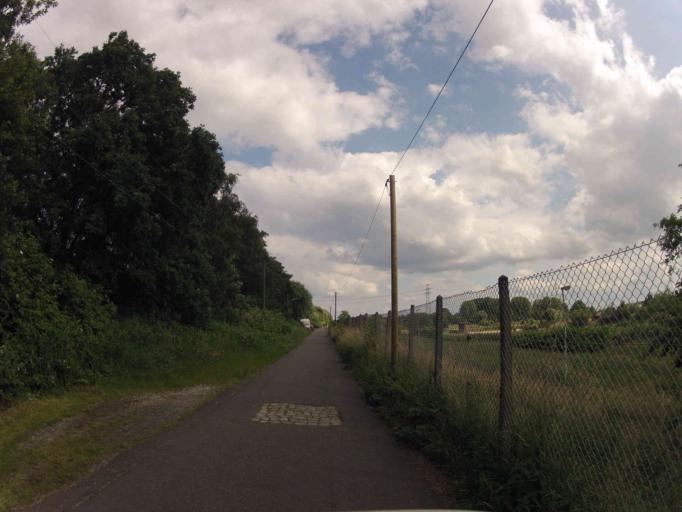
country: DE
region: Hamburg
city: Rothenburgsort
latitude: 53.5261
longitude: 10.0571
